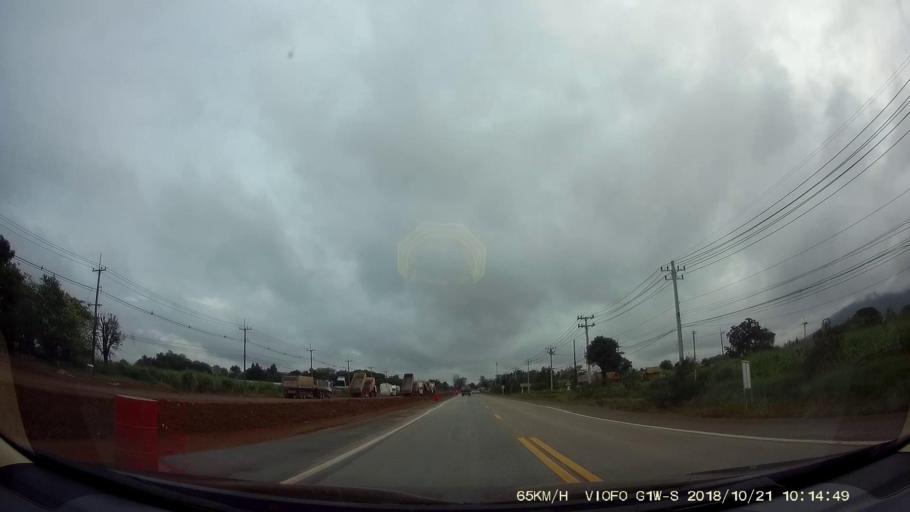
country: TH
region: Chaiyaphum
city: Phu Khiao
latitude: 16.3458
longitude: 102.1599
